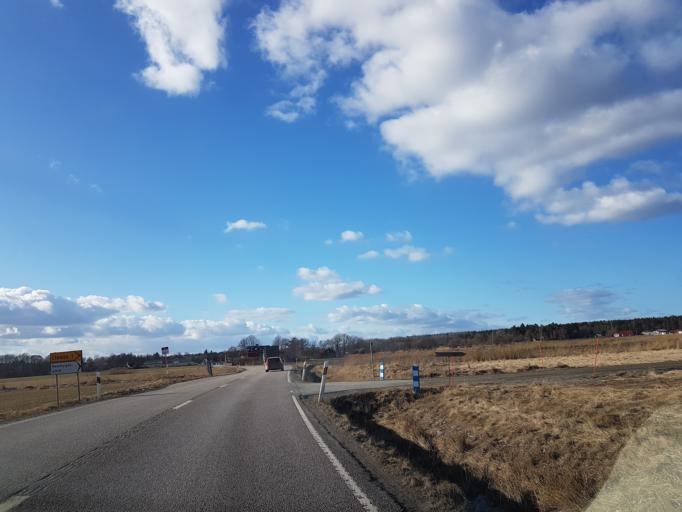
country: SE
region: Stockholm
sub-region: Norrtalje Kommun
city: Rimbo
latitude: 59.7421
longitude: 18.3892
